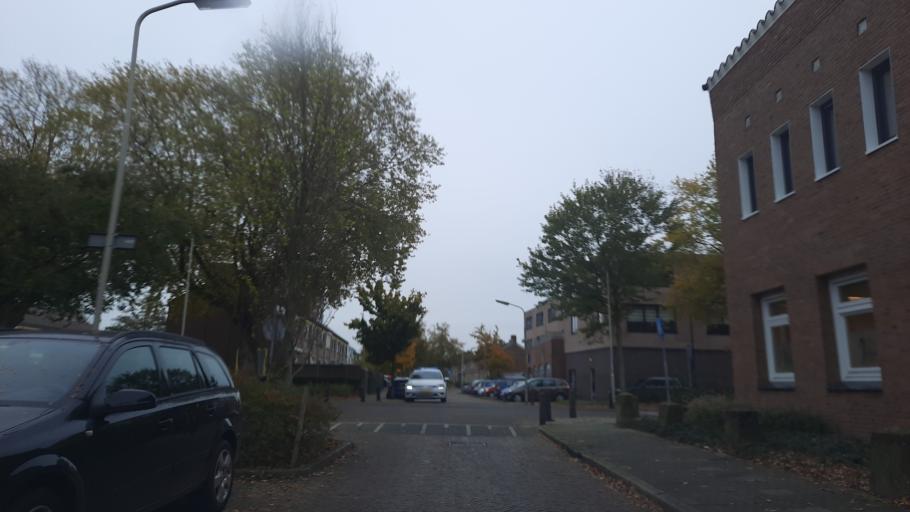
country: NL
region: South Holland
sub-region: Gemeente Gorinchem
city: Gorinchem
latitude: 51.8410
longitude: 4.9643
